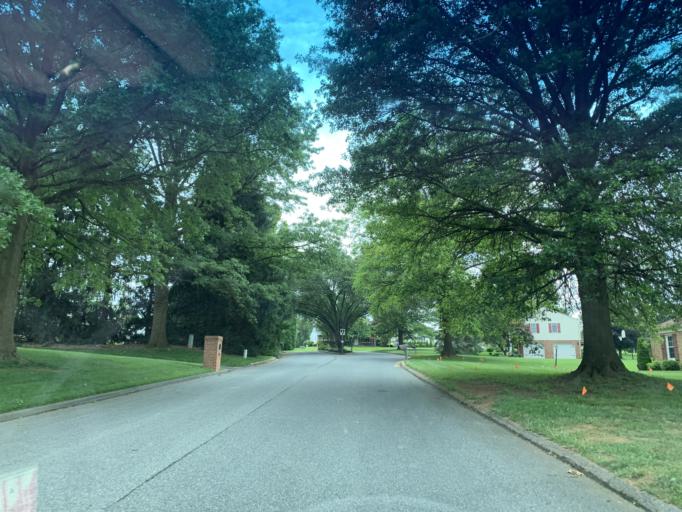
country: US
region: Maryland
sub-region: Harford County
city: Fallston
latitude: 39.5376
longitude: -76.4334
